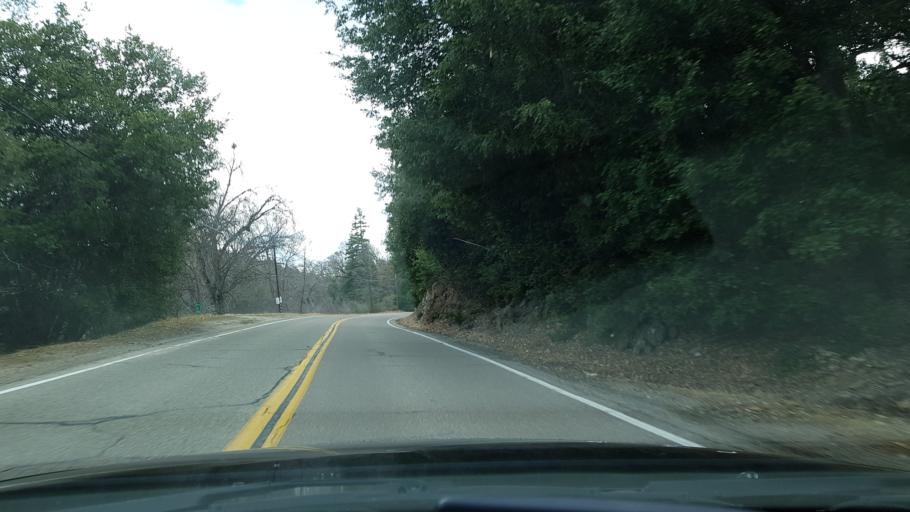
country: US
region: California
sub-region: Riverside County
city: Aguanga
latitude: 33.3235
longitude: -116.8646
